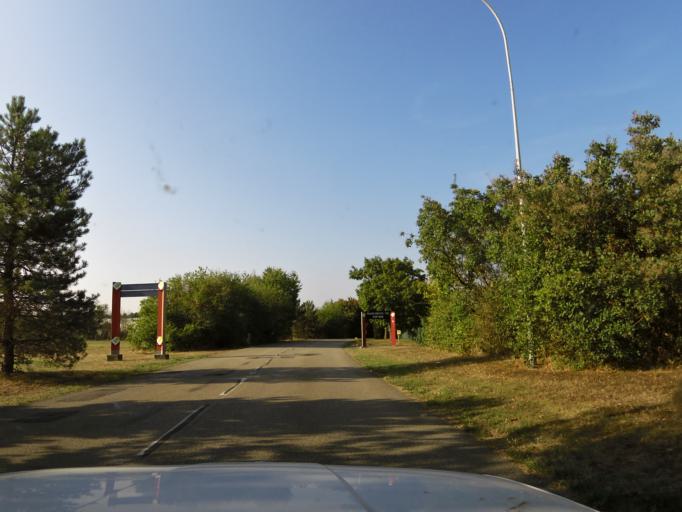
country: FR
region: Rhone-Alpes
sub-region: Departement de l'Ain
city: Saint-Jean-de-Niost
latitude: 45.8415
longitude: 5.2594
